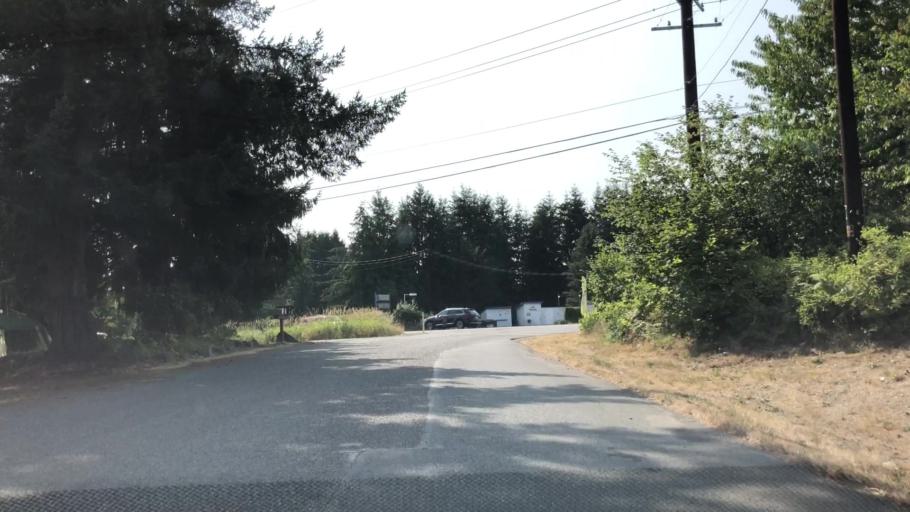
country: US
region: Washington
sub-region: Snohomish County
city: Lochsloy
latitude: 48.0541
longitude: -122.0295
